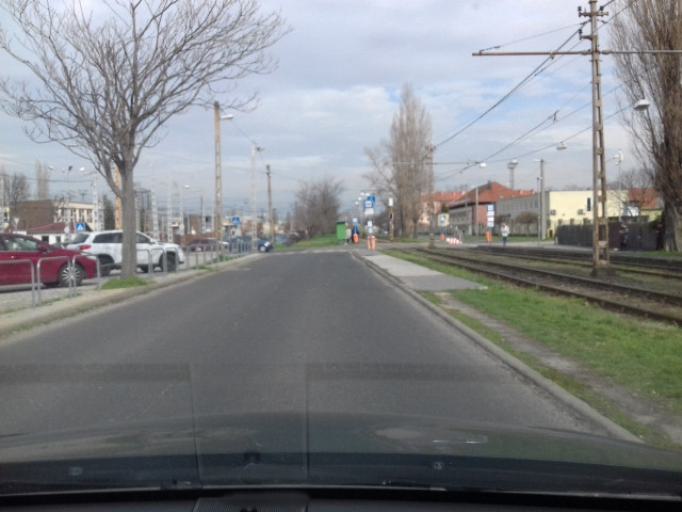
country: HU
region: Budapest
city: Budapest XIV. keruelet
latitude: 47.4906
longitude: 19.1134
